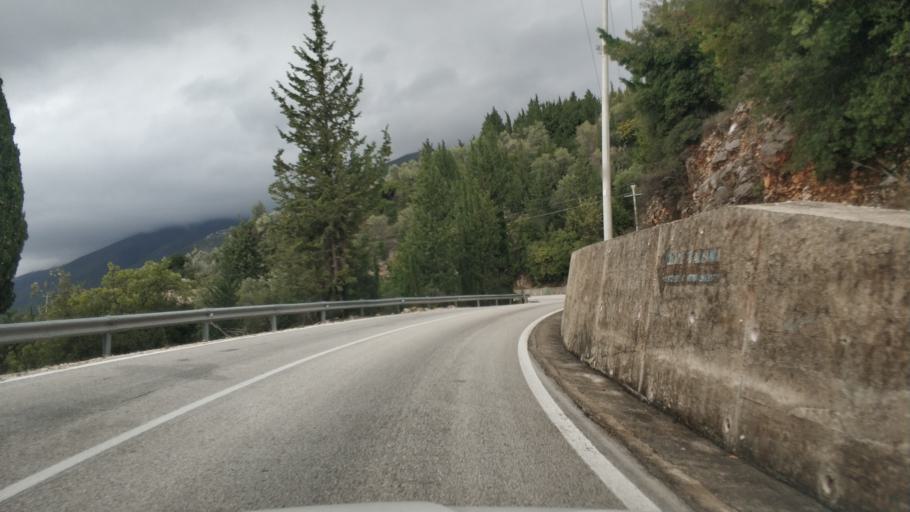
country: AL
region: Vlore
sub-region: Rrethi i Vlores
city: Vranisht
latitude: 40.1696
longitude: 19.6169
